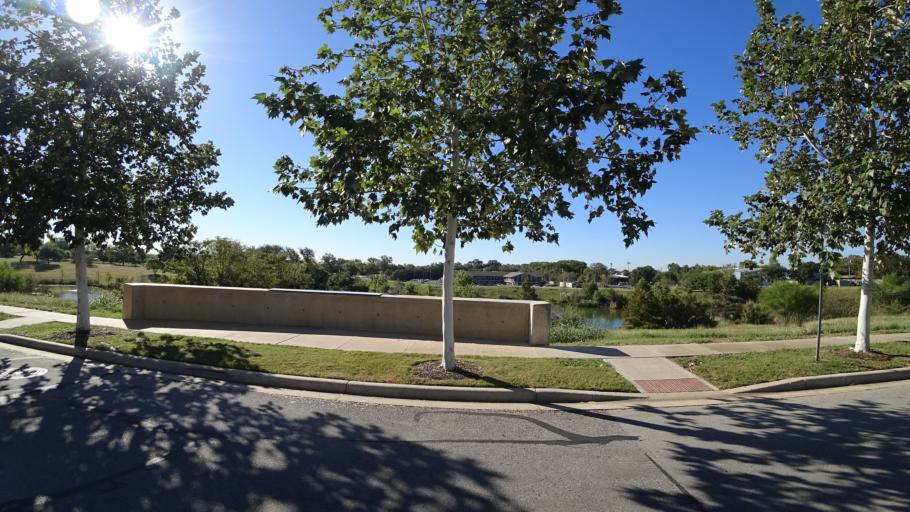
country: US
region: Texas
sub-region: Travis County
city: Austin
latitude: 30.2898
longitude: -97.7026
